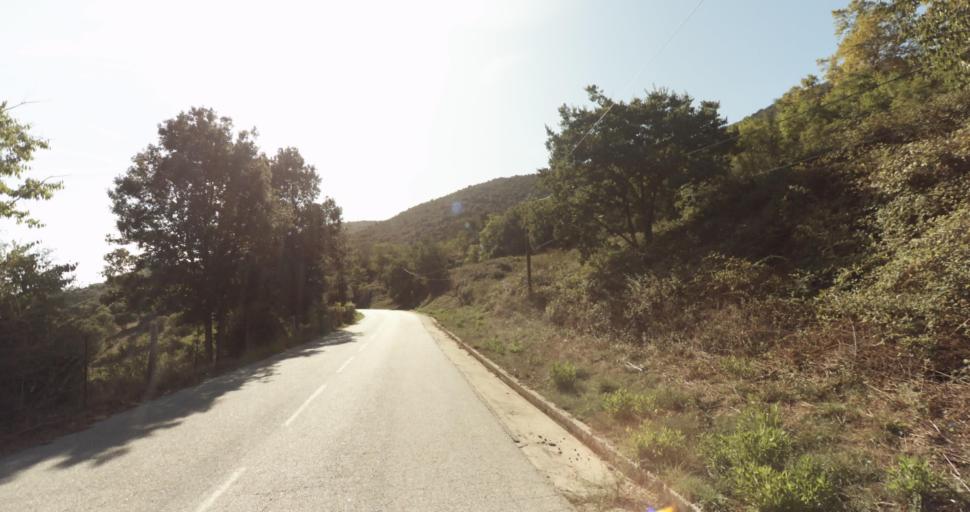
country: FR
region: Corsica
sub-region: Departement de la Corse-du-Sud
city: Ajaccio
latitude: 41.9301
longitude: 8.7017
